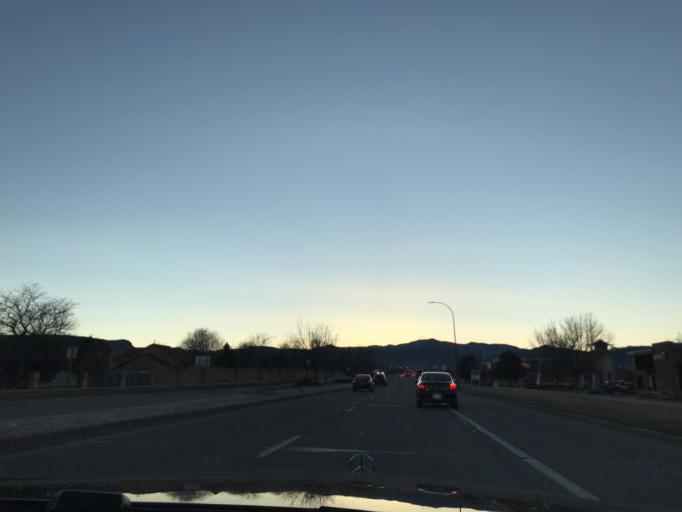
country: US
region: Colorado
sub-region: Jefferson County
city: Applewood
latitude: 39.8126
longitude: -105.1608
